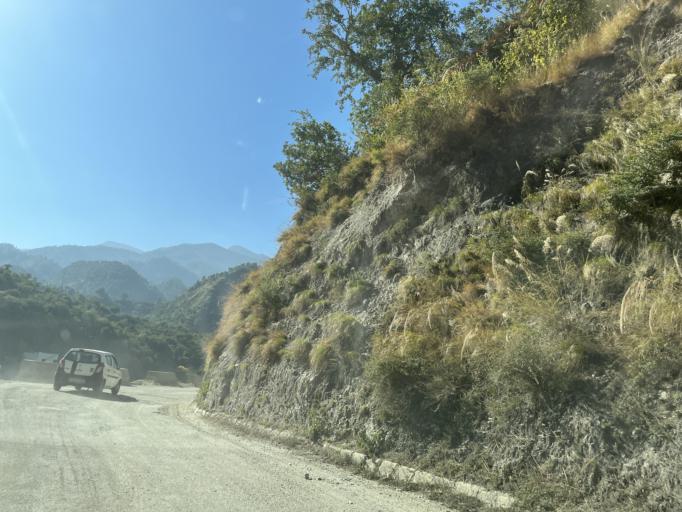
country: IN
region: Uttarakhand
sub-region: Naini Tal
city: Naini Tal
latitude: 29.5096
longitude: 79.4497
